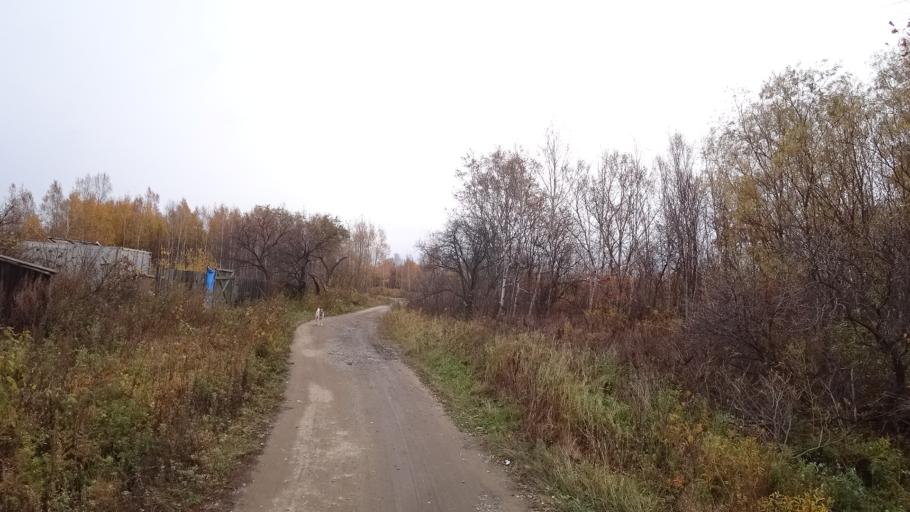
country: RU
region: Khabarovsk Krai
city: Amursk
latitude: 50.1496
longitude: 136.9811
